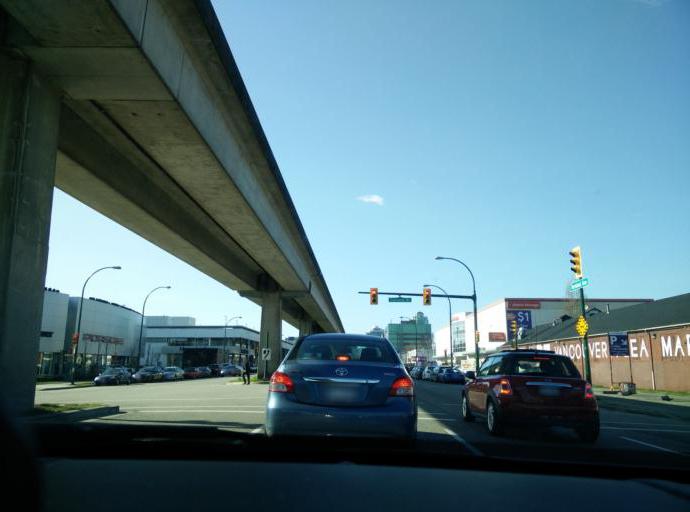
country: CA
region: British Columbia
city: Vancouver
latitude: 49.2711
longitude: -123.0892
